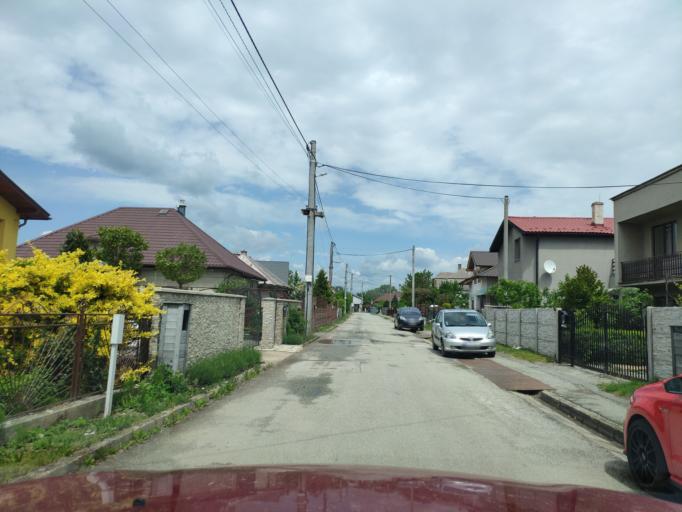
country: SK
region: Kosicky
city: Kosice
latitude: 48.7298
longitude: 21.3392
